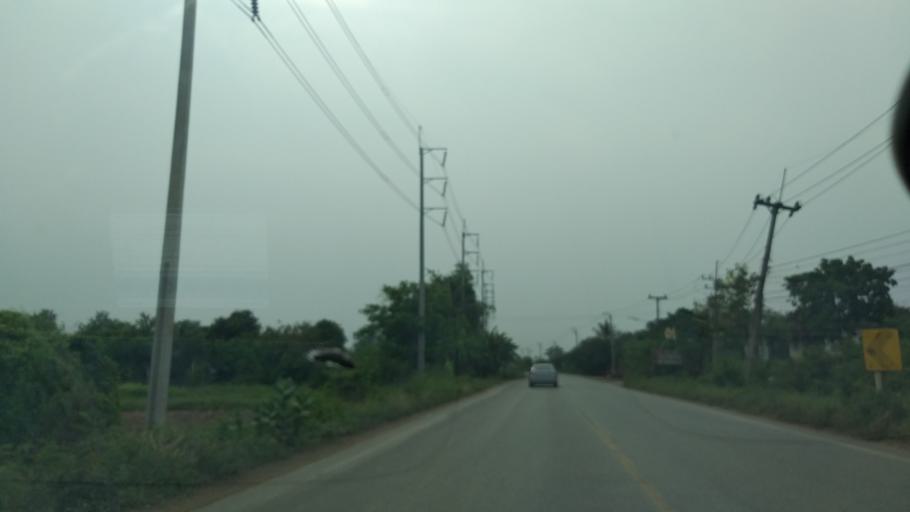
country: TH
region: Chachoengsao
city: Plaeng Yao
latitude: 13.5754
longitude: 101.2552
